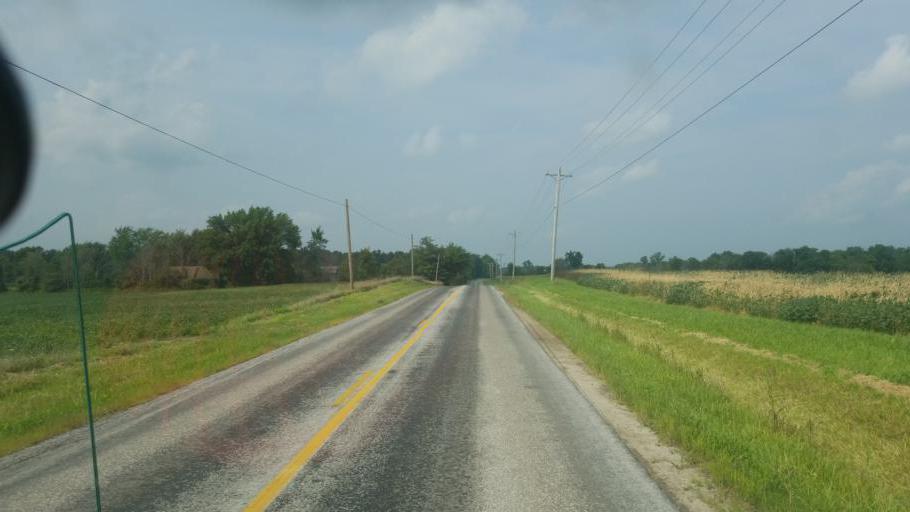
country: US
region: Ohio
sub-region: Wayne County
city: West Salem
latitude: 41.0594
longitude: -82.1627
